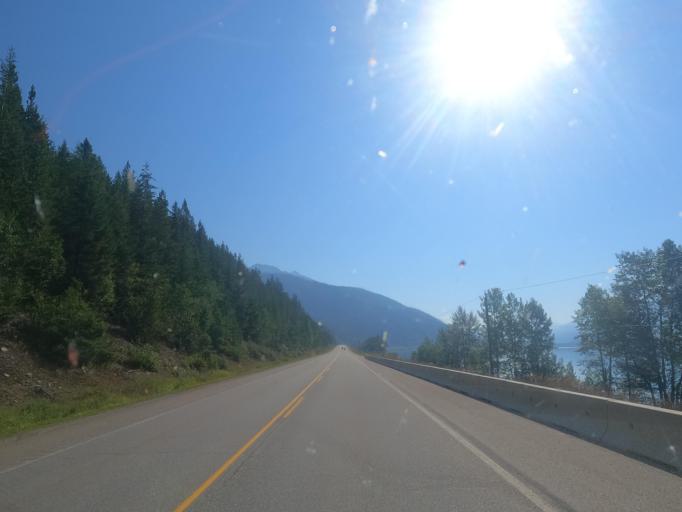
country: CA
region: Alberta
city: Jasper Park Lodge
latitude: 52.9558
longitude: -118.8919
